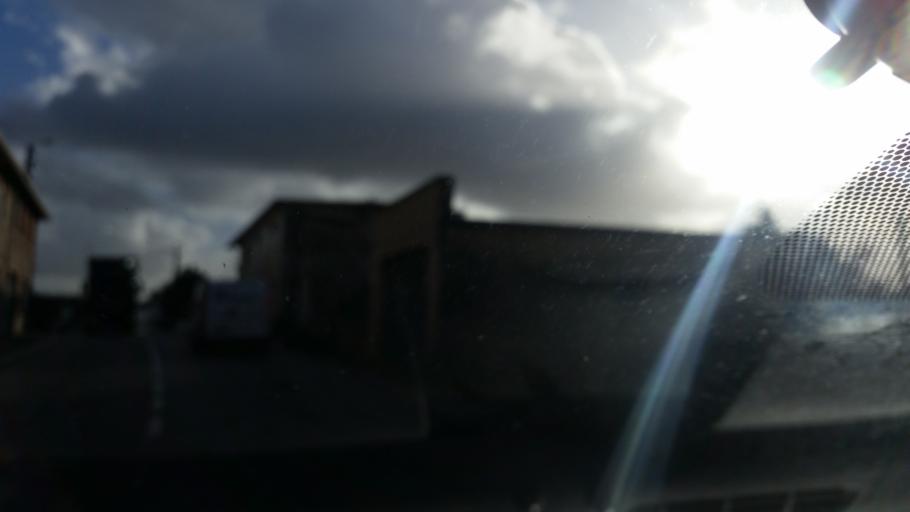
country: PT
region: Braga
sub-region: Guimaraes
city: Lordelo
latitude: 41.3704
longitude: -8.3746
